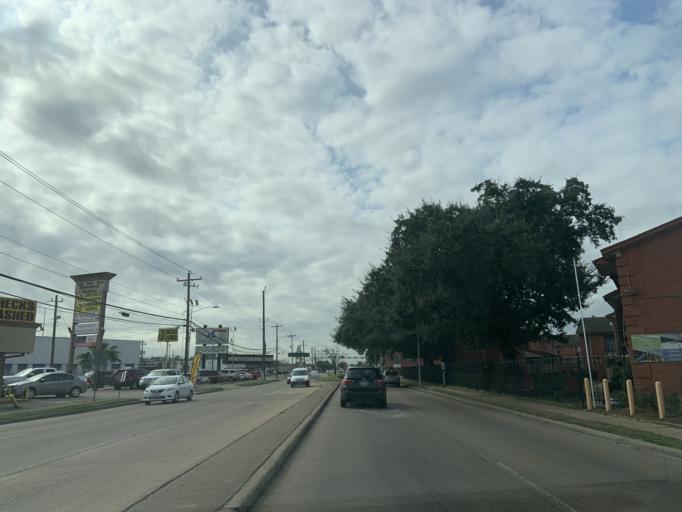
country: US
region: Texas
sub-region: Harris County
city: Bellaire
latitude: 29.6982
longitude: -95.4867
